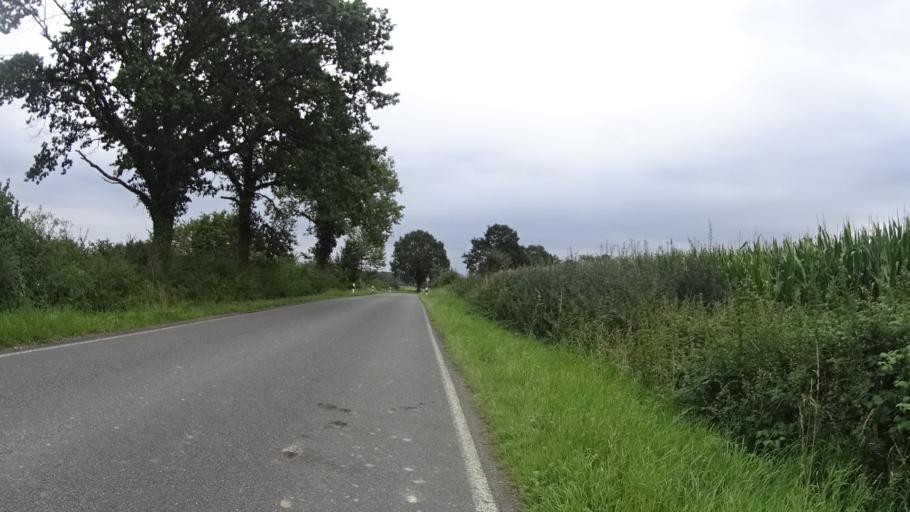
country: DE
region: Schleswig-Holstein
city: Duvensee
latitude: 53.6892
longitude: 10.5743
